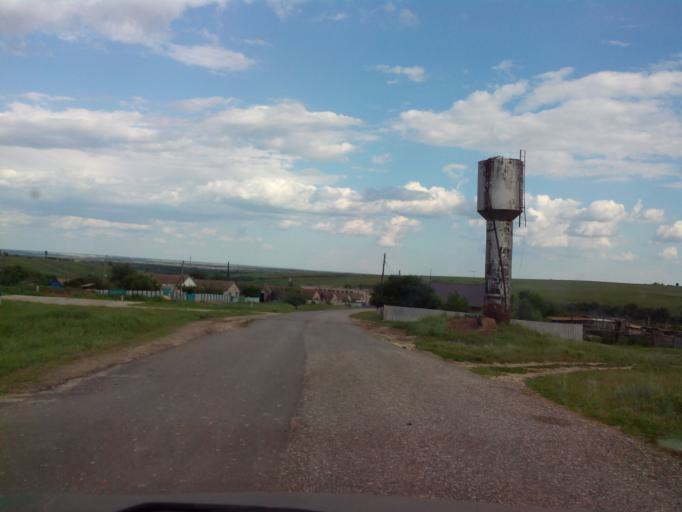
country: RU
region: Volgograd
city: Slashchevskaya
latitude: 49.7805
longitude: 42.4369
